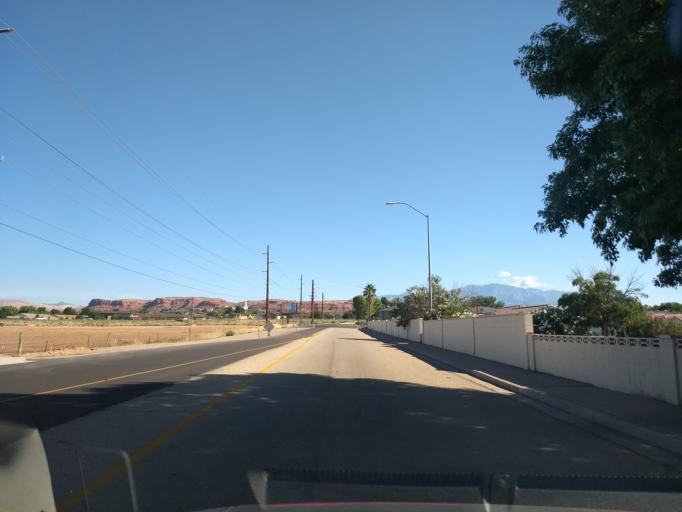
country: US
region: Utah
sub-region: Washington County
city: Saint George
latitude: 37.0875
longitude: -113.5749
